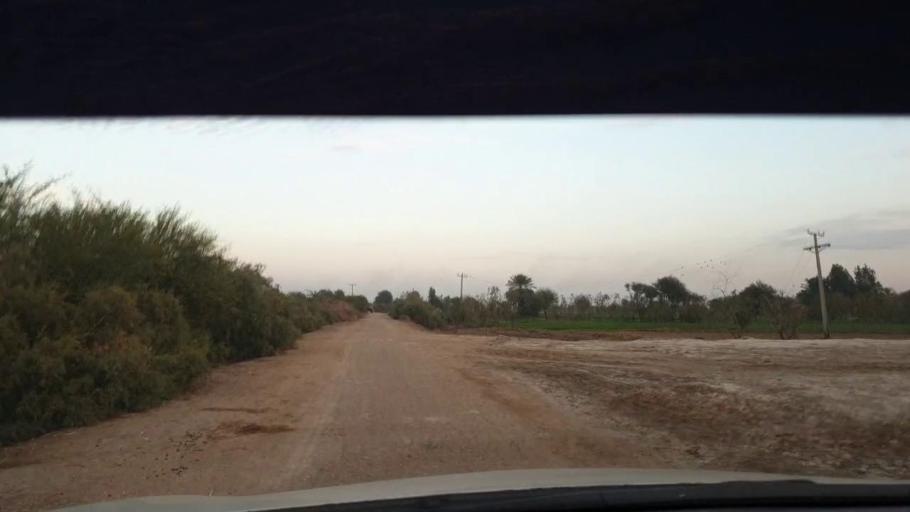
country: PK
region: Sindh
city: Berani
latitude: 25.8007
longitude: 68.8039
